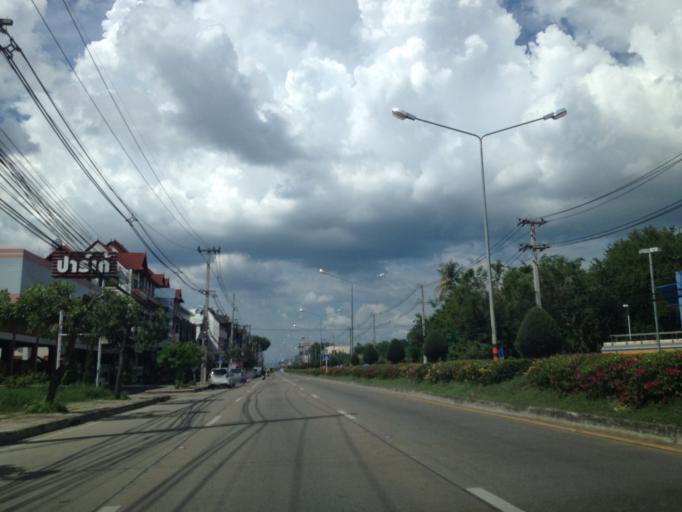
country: TH
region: Chiang Mai
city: Hang Dong
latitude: 18.7308
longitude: 98.9510
